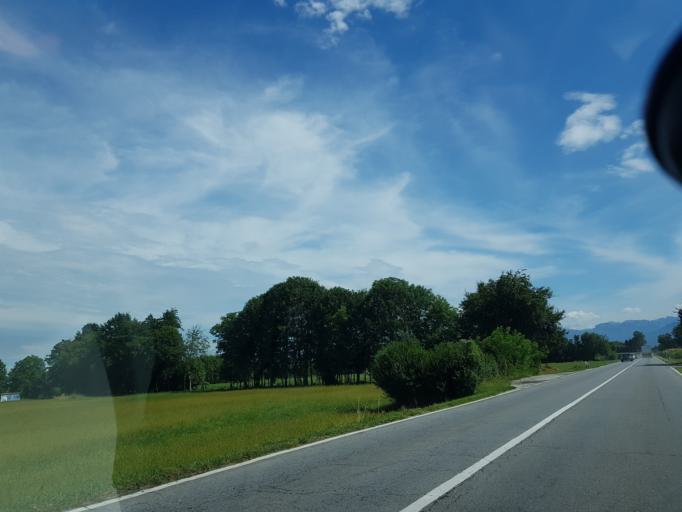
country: IT
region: Piedmont
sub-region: Provincia di Cuneo
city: Roata Rossi
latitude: 44.4521
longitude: 7.5243
